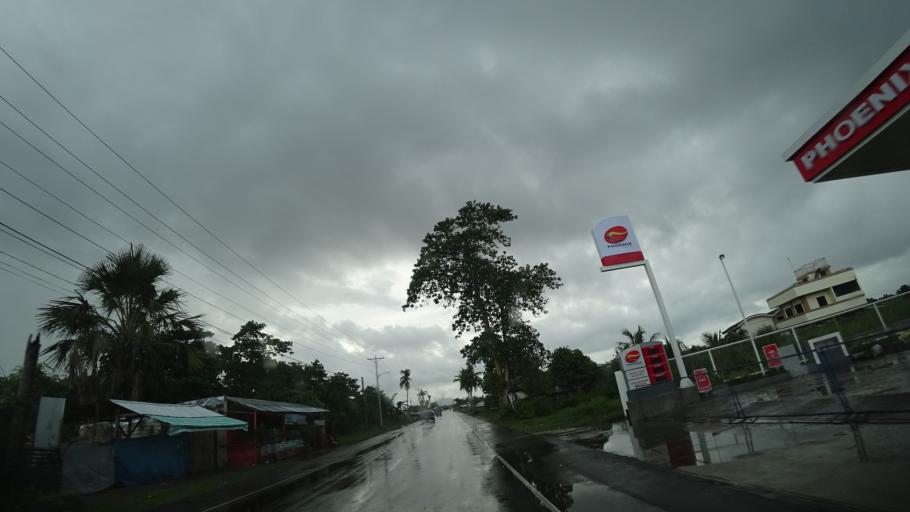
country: PH
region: Eastern Visayas
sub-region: Province of Leyte
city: Tanauan
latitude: 11.1158
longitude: 125.0181
